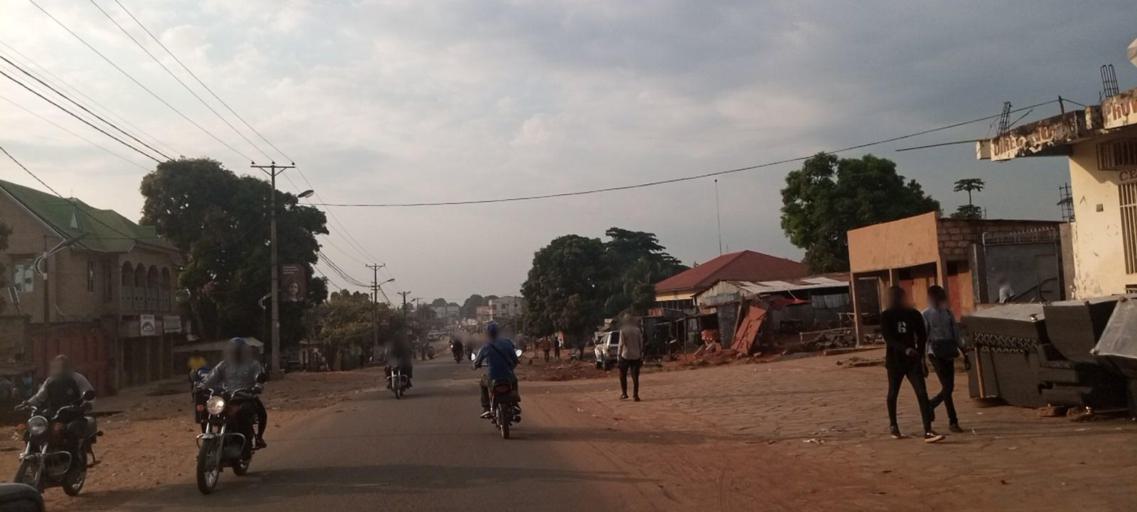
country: CD
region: Kasai-Oriental
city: Mbuji-Mayi
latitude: -6.1320
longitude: 23.6069
